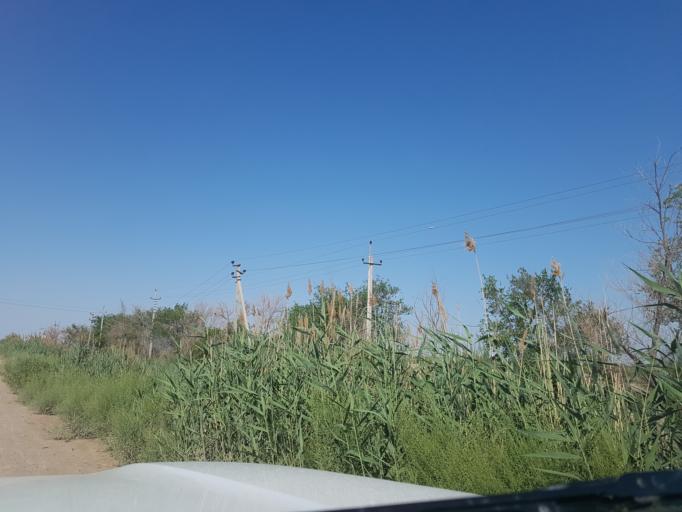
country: TM
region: Dasoguz
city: Koeneuergench
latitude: 42.1362
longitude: 58.9541
